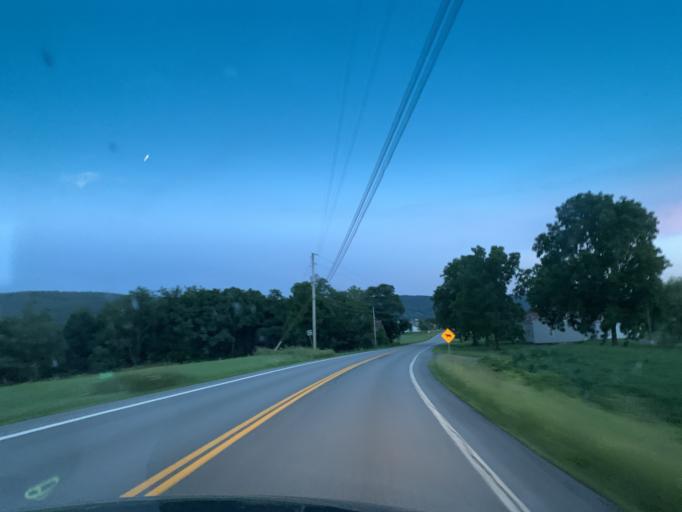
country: US
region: New York
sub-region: Chenango County
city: New Berlin
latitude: 42.5878
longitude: -75.3353
